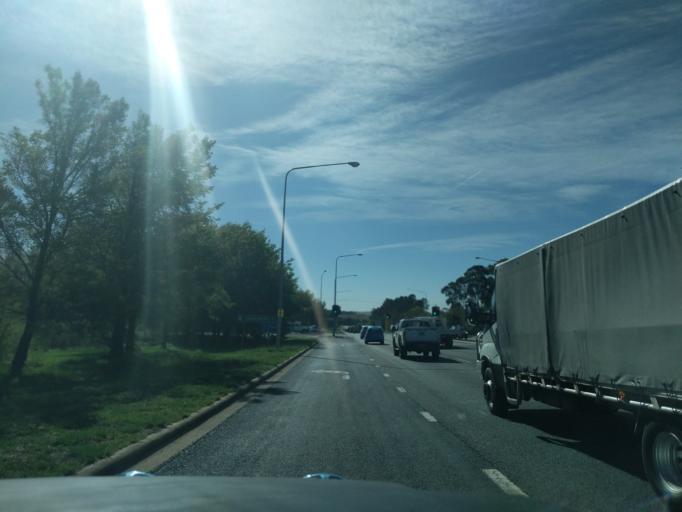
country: AU
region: Australian Capital Territory
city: Forrest
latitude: -35.3433
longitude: 149.1532
